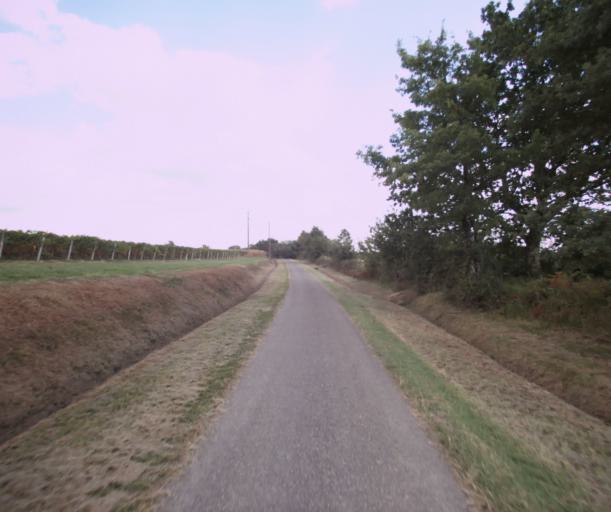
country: FR
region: Midi-Pyrenees
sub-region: Departement du Gers
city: Cazaubon
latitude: 43.8867
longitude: -0.0559
